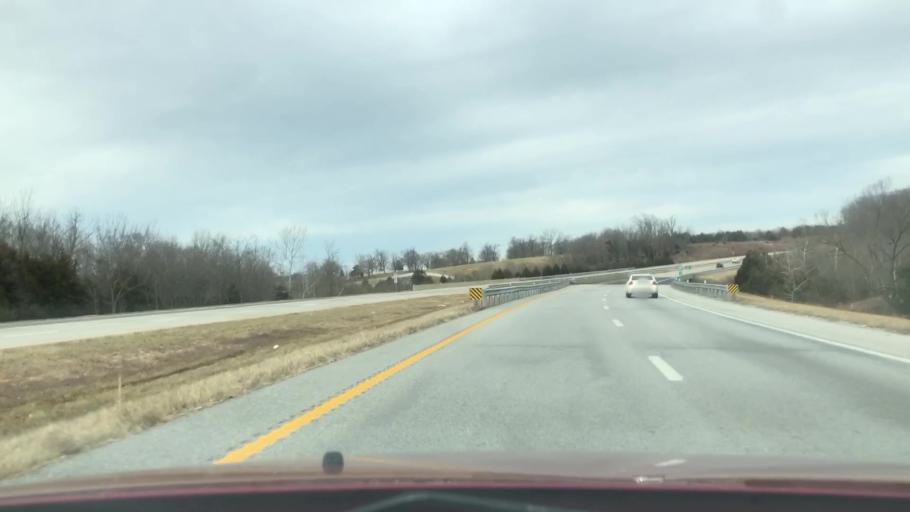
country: US
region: Missouri
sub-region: Greene County
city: Springfield
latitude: 37.2623
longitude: -93.2248
